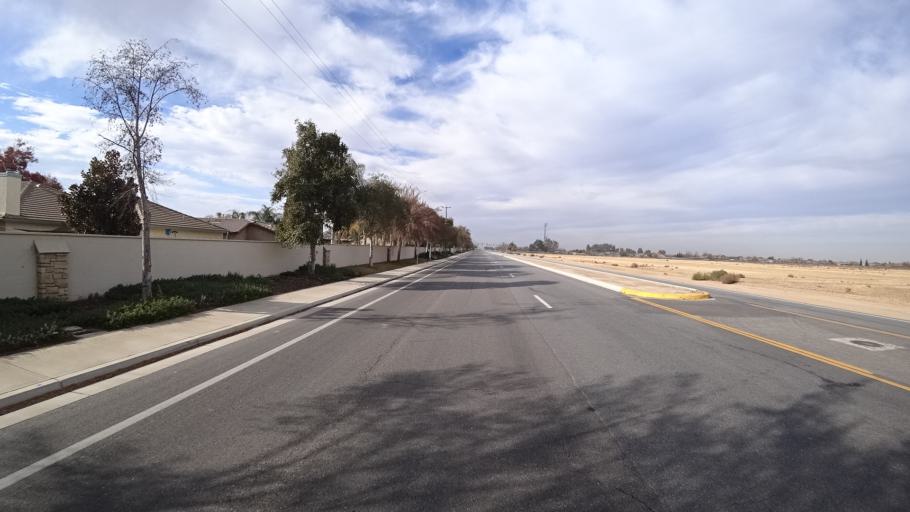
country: US
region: California
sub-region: Kern County
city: Greenacres
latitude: 35.4270
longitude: -119.1150
